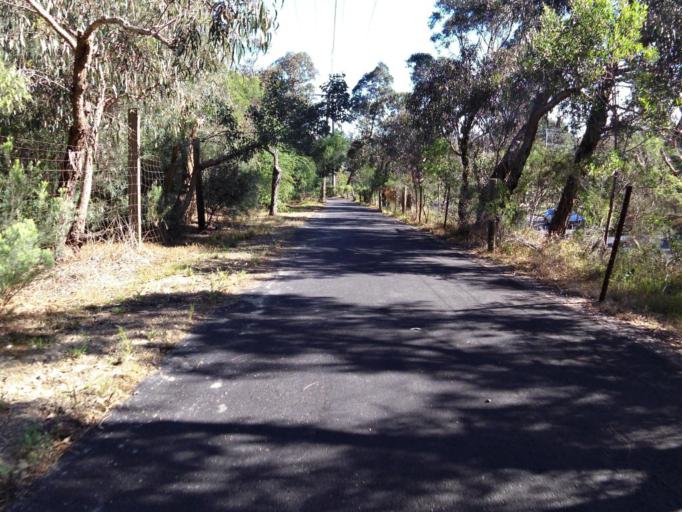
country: AU
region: Victoria
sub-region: Nillumbik
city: Eltham
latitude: -37.7370
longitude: 145.1345
